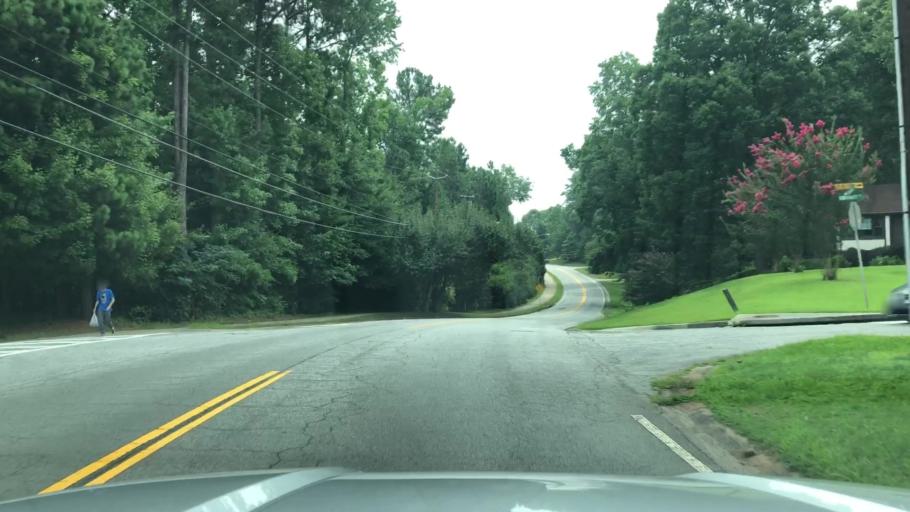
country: US
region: Georgia
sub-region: Cobb County
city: Smyrna
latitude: 33.8648
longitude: -84.5426
